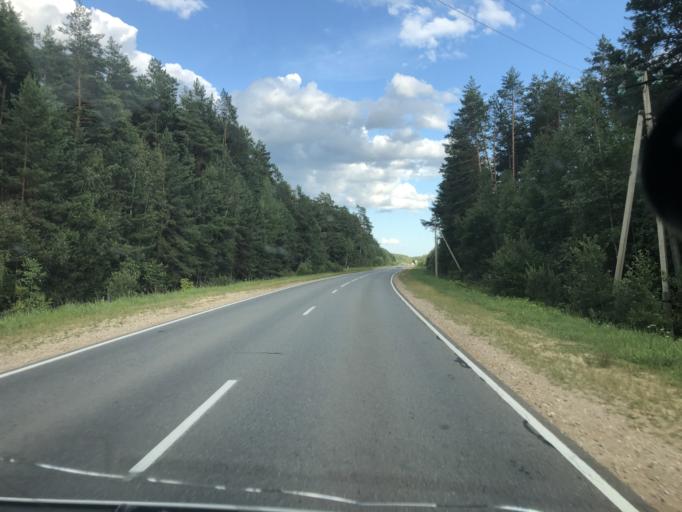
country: RU
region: Kaluga
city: Yukhnov
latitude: 54.7227
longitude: 35.2169
